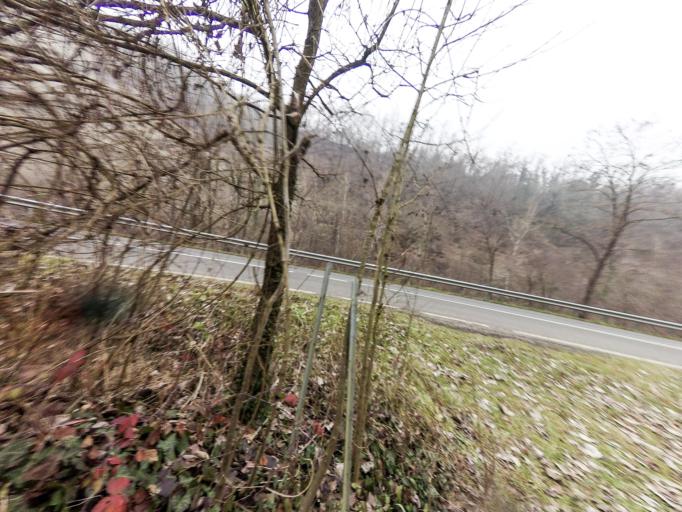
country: IT
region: Emilia-Romagna
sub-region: Provincia di Bologna
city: Pianoro
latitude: 44.3410
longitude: 11.3188
